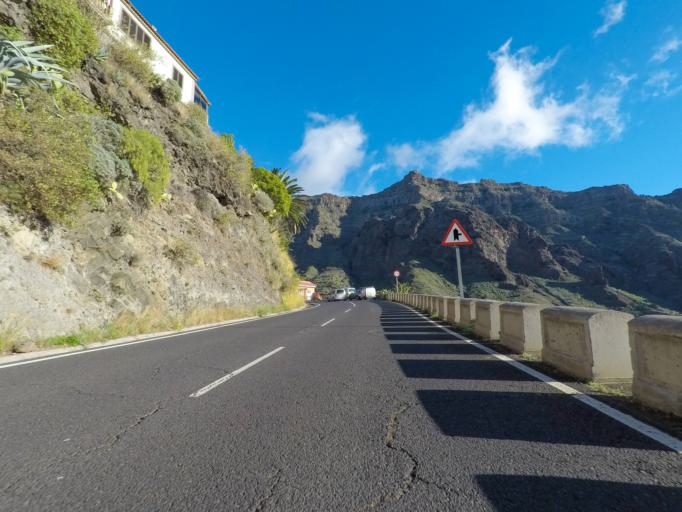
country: ES
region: Canary Islands
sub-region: Provincia de Santa Cruz de Tenerife
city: Vallehermosa
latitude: 28.1164
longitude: -17.3128
